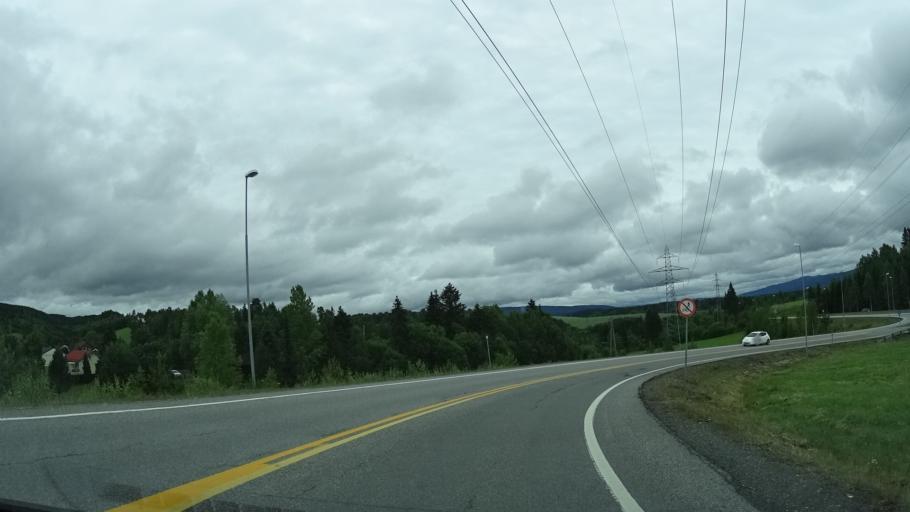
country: NO
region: Buskerud
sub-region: Ringerike
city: Honefoss
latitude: 60.1747
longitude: 10.2185
